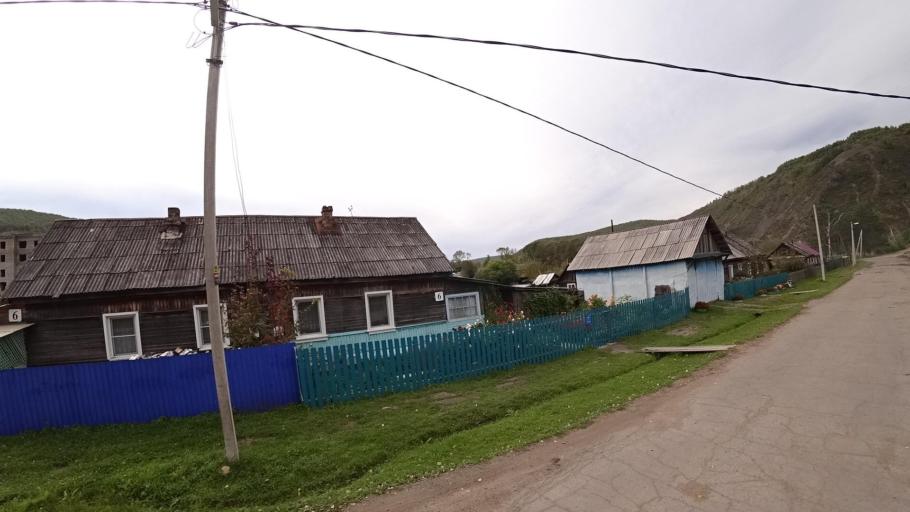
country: RU
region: Jewish Autonomous Oblast
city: Khingansk
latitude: 49.1280
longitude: 131.1994
